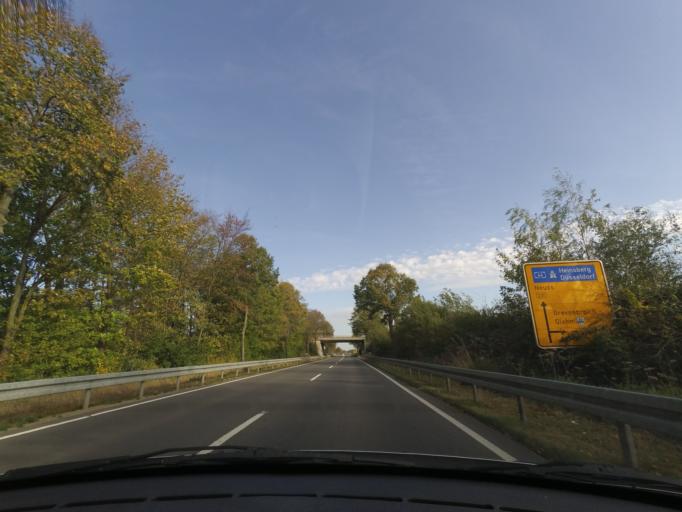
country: DE
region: North Rhine-Westphalia
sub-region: Regierungsbezirk Dusseldorf
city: Neubrueck
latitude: 51.1719
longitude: 6.5909
